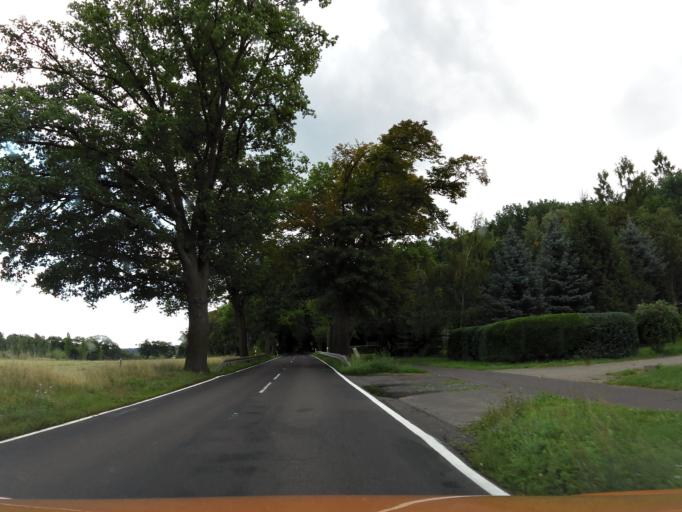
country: DE
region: Brandenburg
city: Potsdam
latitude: 52.4544
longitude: 13.0417
